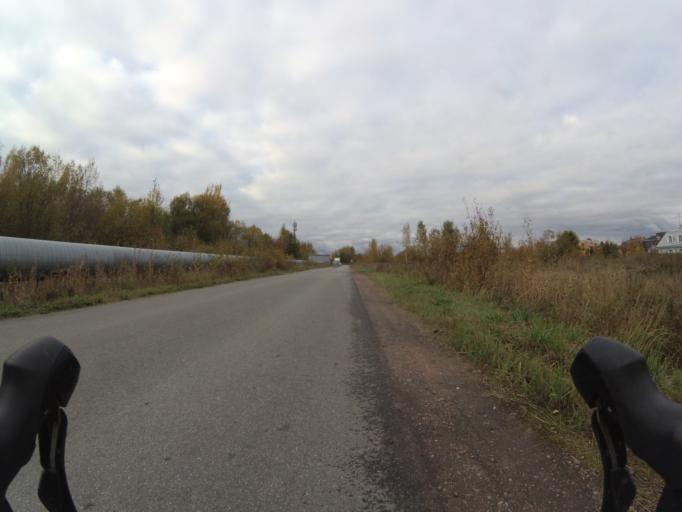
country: RU
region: St.-Petersburg
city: Lakhtinskiy
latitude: 60.0000
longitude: 30.1567
